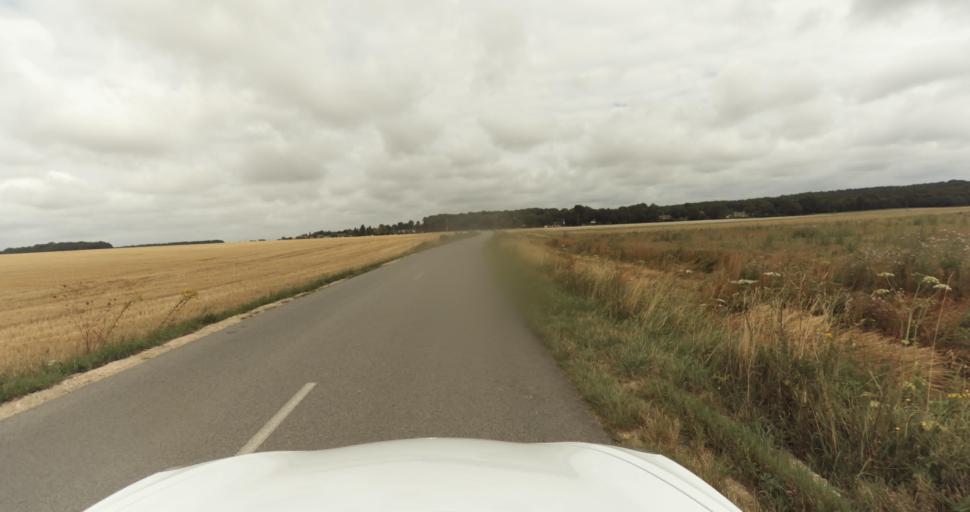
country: FR
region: Haute-Normandie
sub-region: Departement de l'Eure
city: Claville
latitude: 49.0149
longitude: 1.0341
